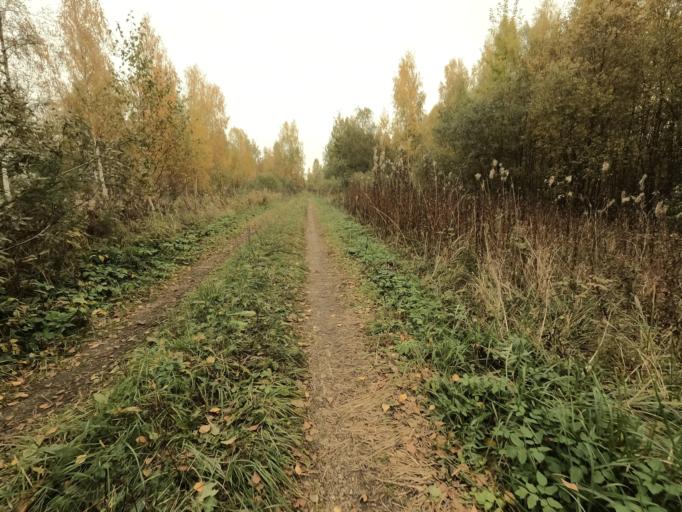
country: RU
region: Novgorod
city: Pankovka
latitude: 58.8739
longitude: 30.9388
